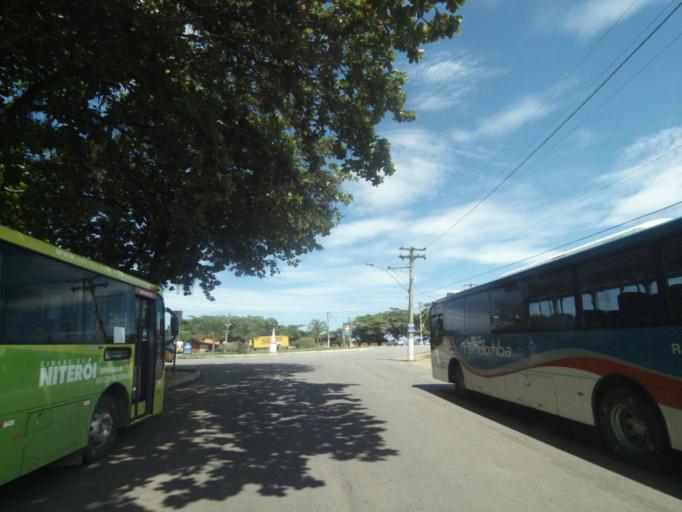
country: BR
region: Rio de Janeiro
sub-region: Niteroi
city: Niteroi
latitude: -22.9701
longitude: -43.0443
